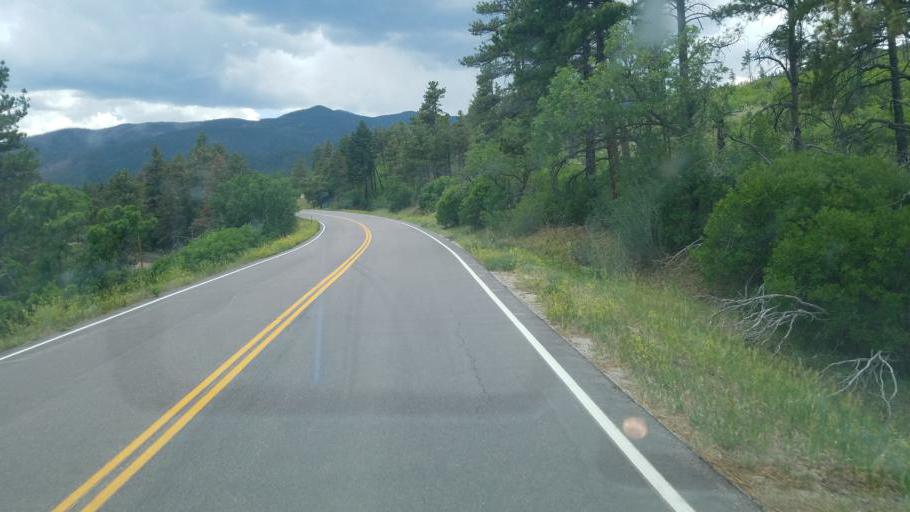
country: US
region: Colorado
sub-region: Fremont County
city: Florence
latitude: 38.1935
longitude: -105.1041
